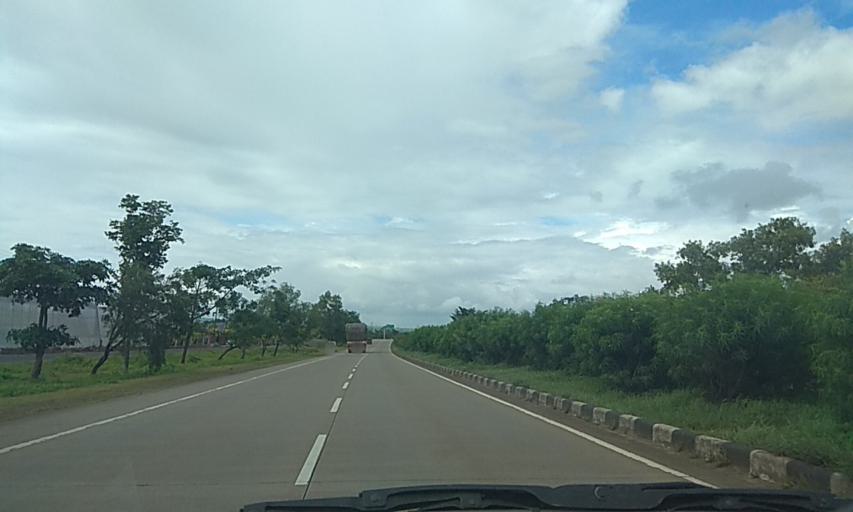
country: IN
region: Maharashtra
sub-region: Kolhapur
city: Kagal
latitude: 16.5345
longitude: 74.3195
